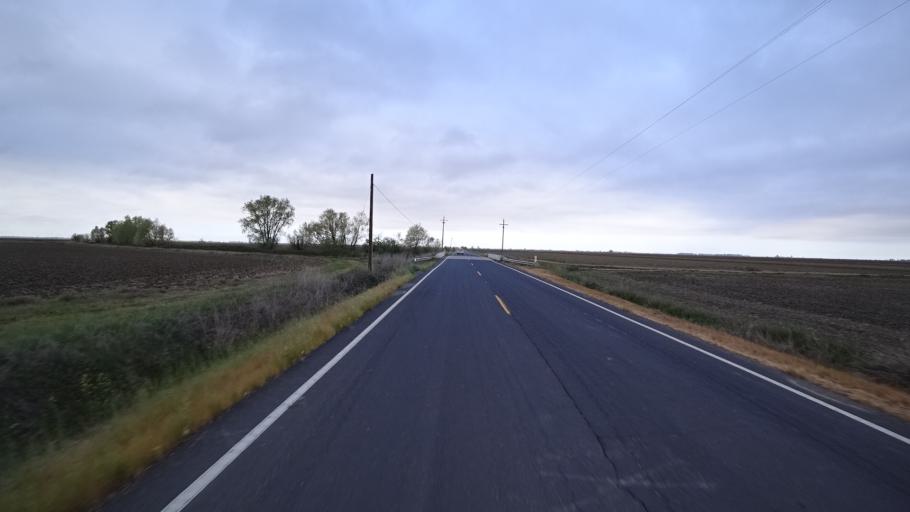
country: US
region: California
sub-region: Glenn County
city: Willows
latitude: 39.4063
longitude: -122.0552
